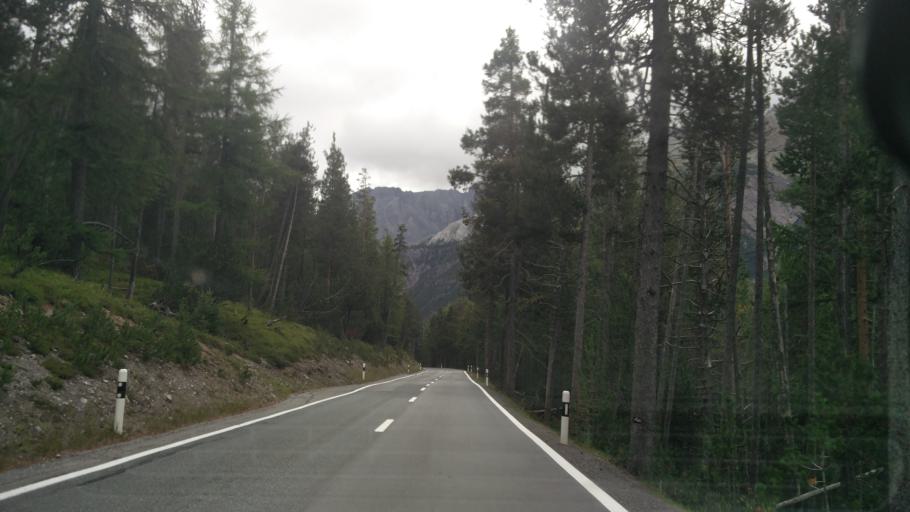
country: CH
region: Grisons
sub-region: Inn District
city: Zernez
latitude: 46.6705
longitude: 10.1660
